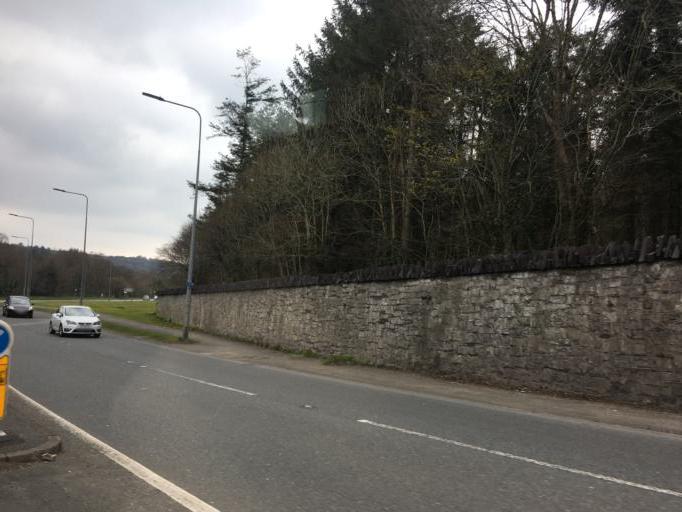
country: GB
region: Wales
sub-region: Gwynedd
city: Y Felinheli
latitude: 53.1968
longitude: -4.1826
